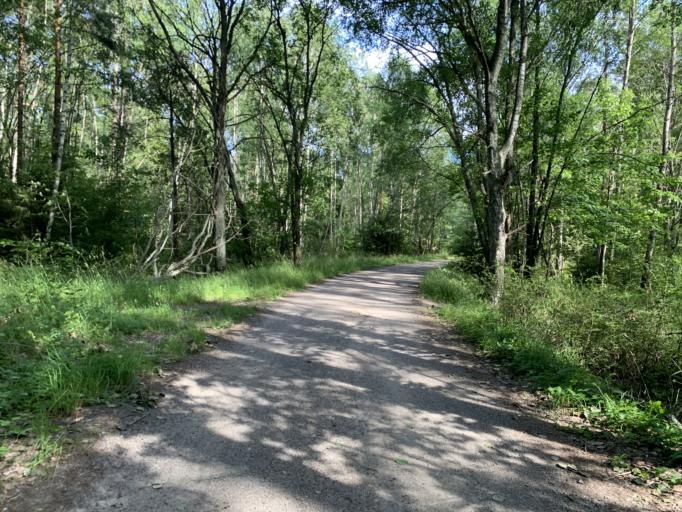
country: SE
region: Stockholm
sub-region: Stockholms Kommun
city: Kista
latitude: 59.3980
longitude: 17.9687
